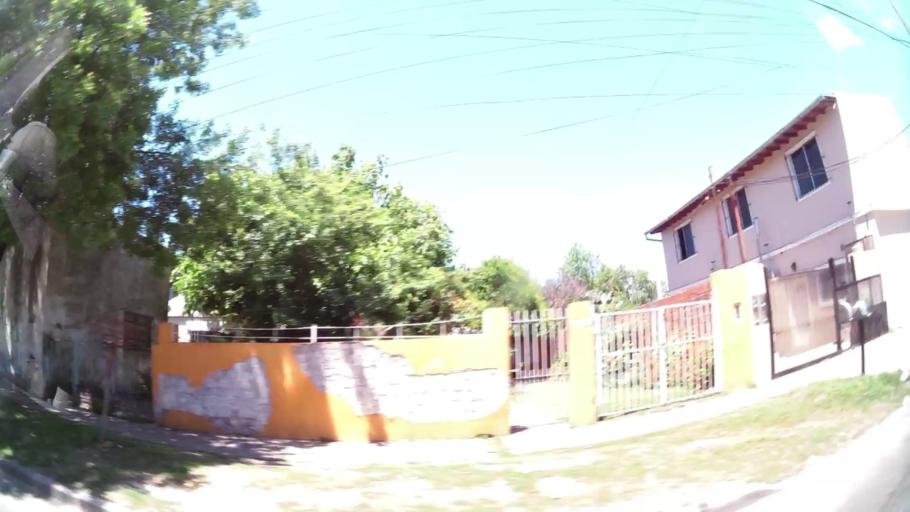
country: AR
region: Buenos Aires
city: Hurlingham
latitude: -34.5049
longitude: -58.7051
